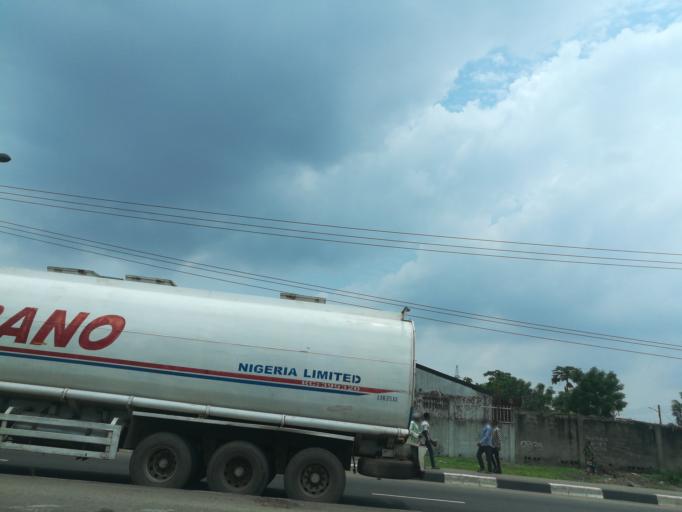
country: NG
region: Lagos
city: Ojota
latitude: 6.5853
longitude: 3.3771
